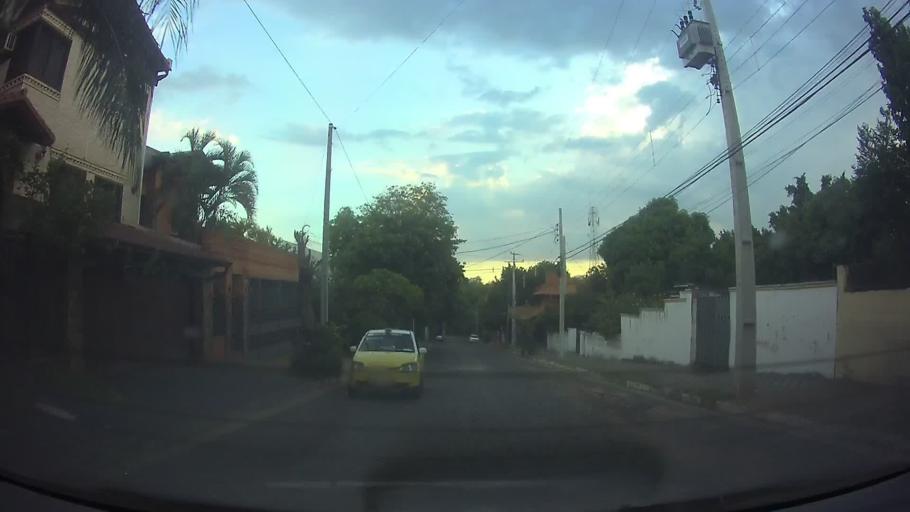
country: PY
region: Asuncion
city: Asuncion
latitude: -25.2683
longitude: -57.5709
